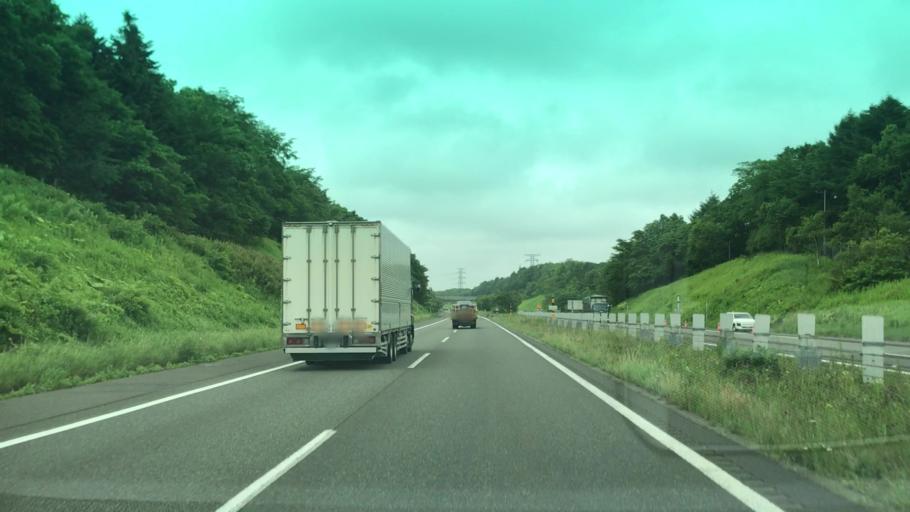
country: JP
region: Hokkaido
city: Chitose
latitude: 42.7275
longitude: 141.6530
